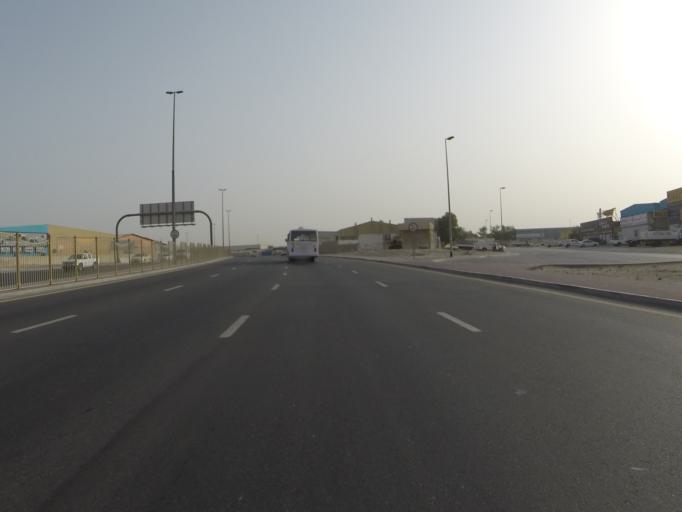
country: AE
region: Dubai
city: Dubai
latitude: 25.1176
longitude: 55.2122
